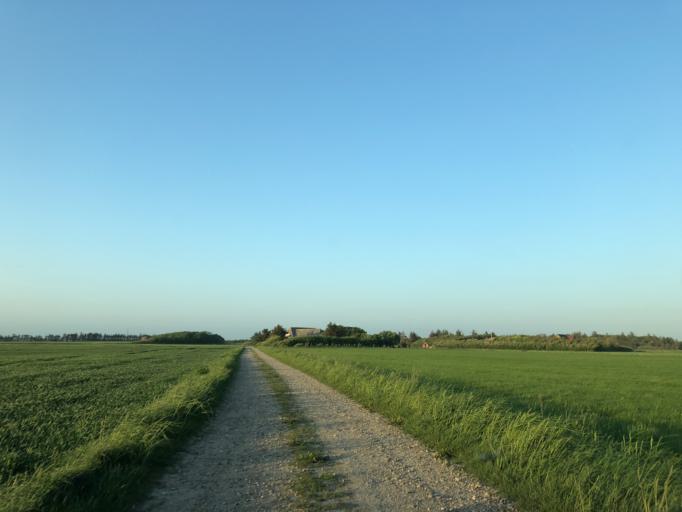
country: DK
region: Central Jutland
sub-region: Holstebro Kommune
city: Ulfborg
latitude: 56.2511
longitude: 8.1542
